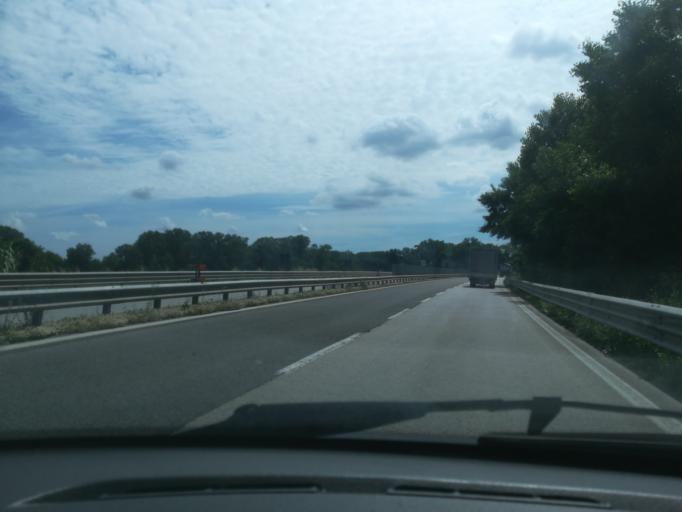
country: IT
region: The Marches
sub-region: Provincia di Macerata
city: Corridonia
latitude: 43.2684
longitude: 13.5185
